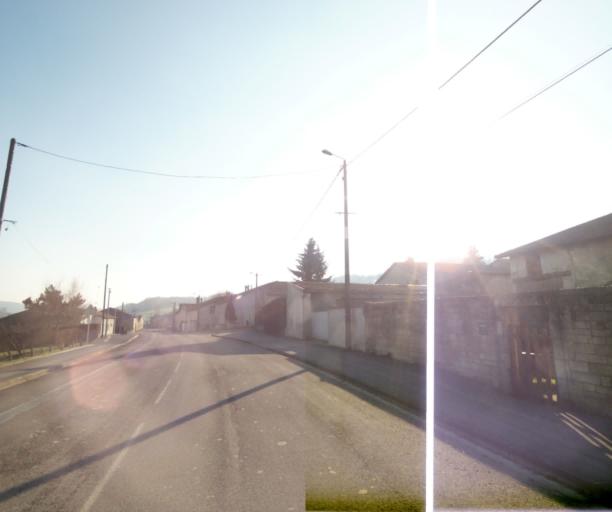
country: FR
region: Champagne-Ardenne
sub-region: Departement de la Haute-Marne
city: Chevillon
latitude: 48.5070
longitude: 5.1134
